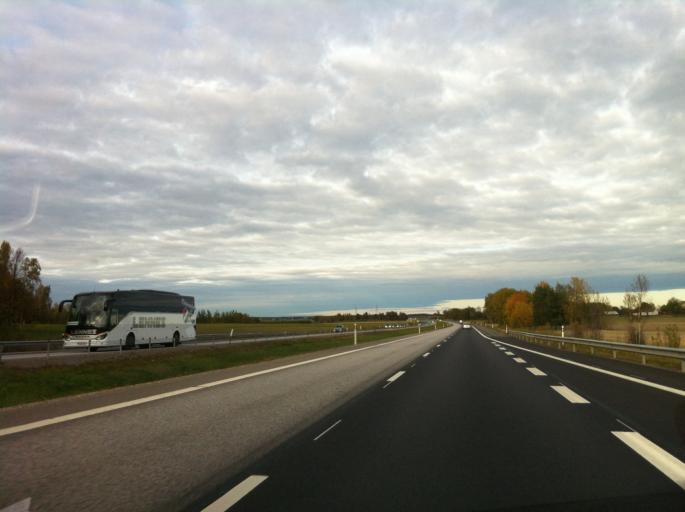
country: SE
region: OErebro
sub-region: Hallsbergs Kommun
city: Hallsberg
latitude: 59.1196
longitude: 15.0710
